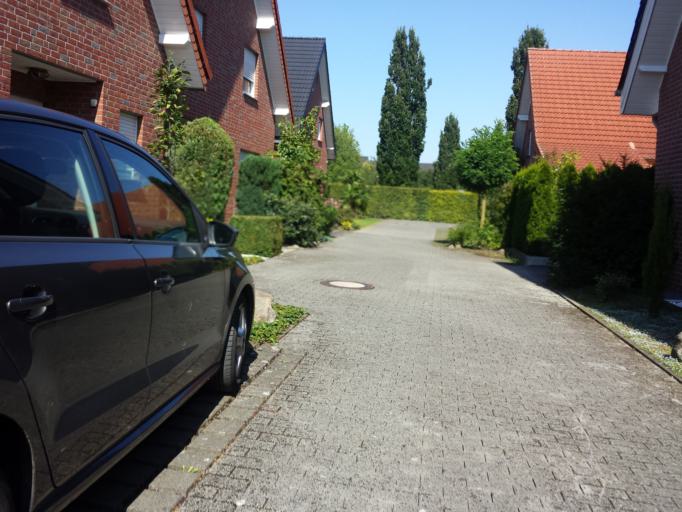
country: DE
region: North Rhine-Westphalia
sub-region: Regierungsbezirk Detmold
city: Guetersloh
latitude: 51.8886
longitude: 8.3665
